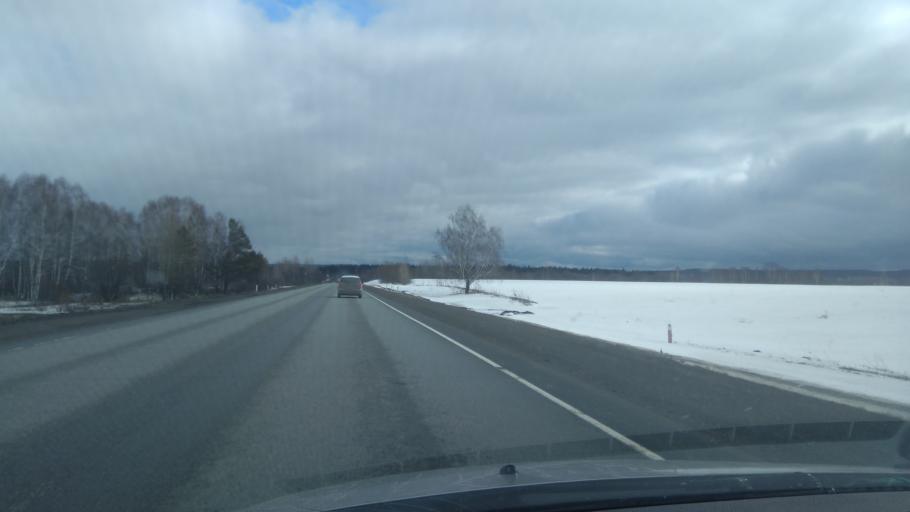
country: RU
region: Sverdlovsk
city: Ufimskiy
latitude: 56.7723
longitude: 58.0741
